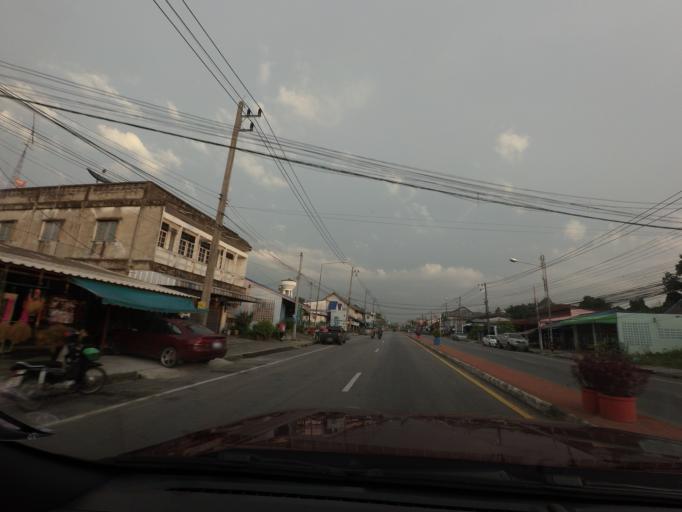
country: TH
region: Pattani
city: Mae Lan
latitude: 6.5809
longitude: 101.1979
